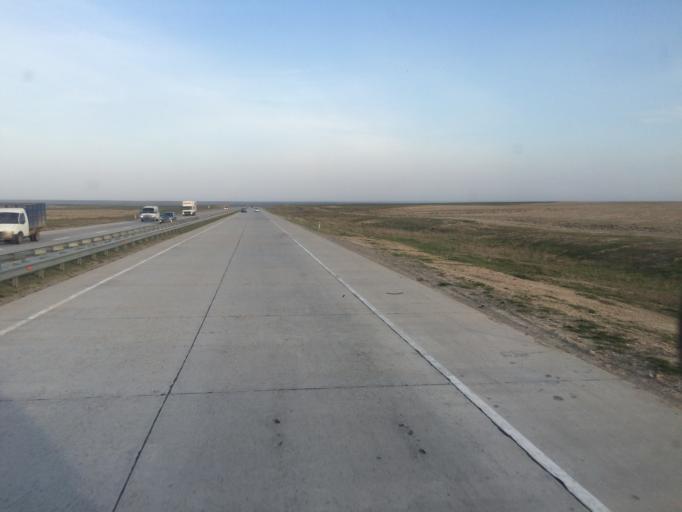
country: KZ
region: Ongtustik Qazaqstan
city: Temirlanovka
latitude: 42.6469
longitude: 69.2447
